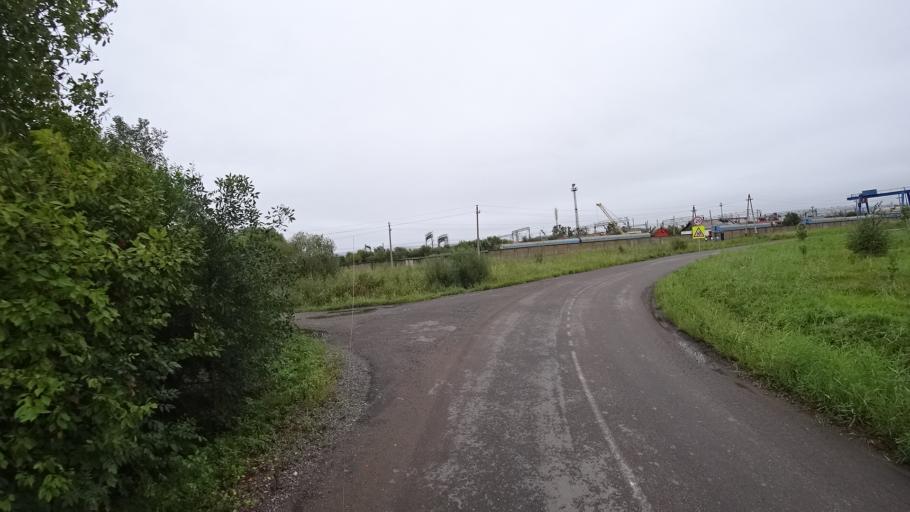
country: RU
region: Primorskiy
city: Monastyrishche
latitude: 44.2102
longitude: 132.4377
